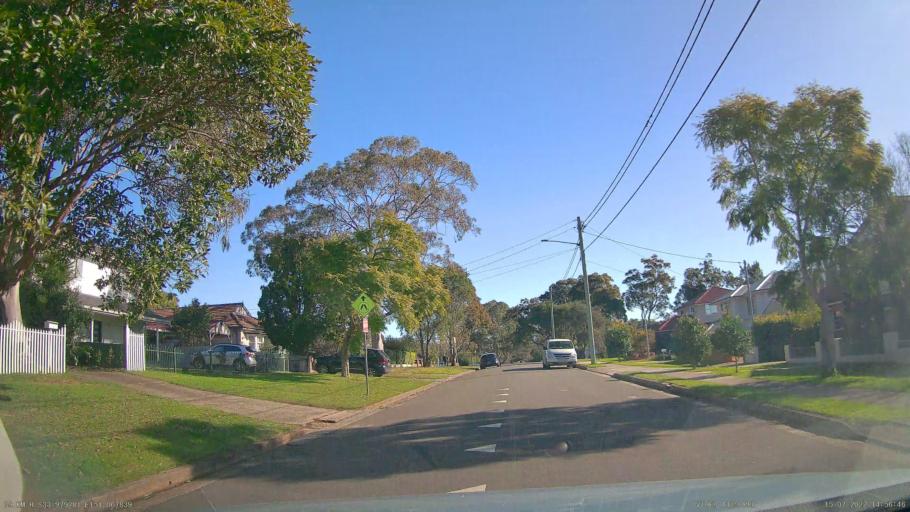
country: AU
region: New South Wales
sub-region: Hurstville
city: Oatley
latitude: -33.9793
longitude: 151.0677
